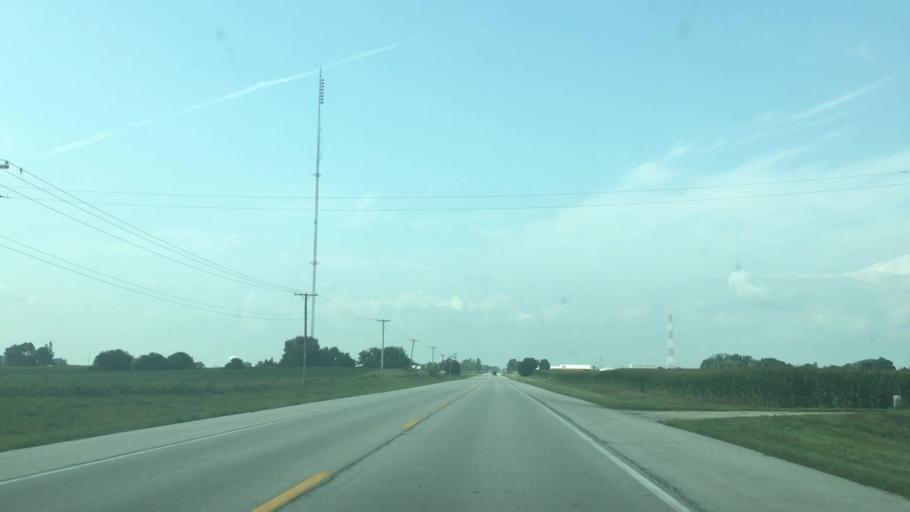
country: US
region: Illinois
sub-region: DeKalb County
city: DeKalb
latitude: 41.8716
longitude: -88.7538
